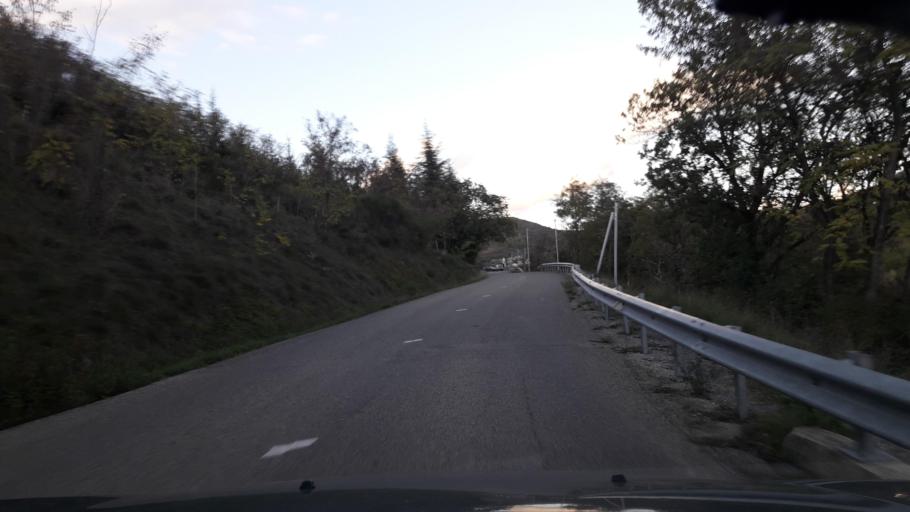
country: FR
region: Rhone-Alpes
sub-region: Departement de l'Ardeche
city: Vesseaux
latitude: 44.6340
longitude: 4.4967
